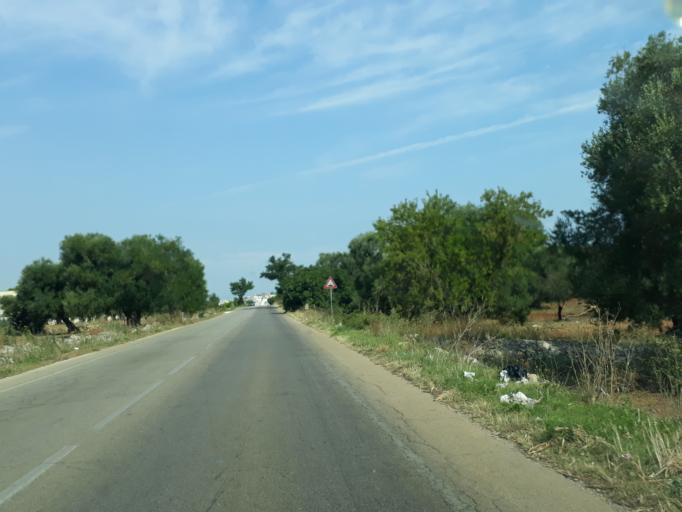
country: IT
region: Apulia
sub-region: Provincia di Brindisi
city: Carovigno
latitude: 40.6897
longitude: 17.6747
